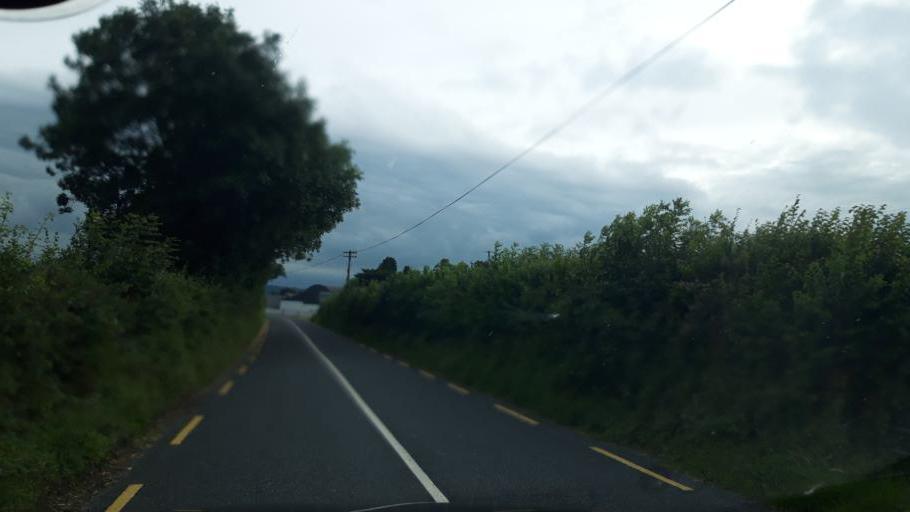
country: IE
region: Leinster
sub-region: Kilkenny
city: Ballyragget
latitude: 52.7555
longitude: -7.3913
